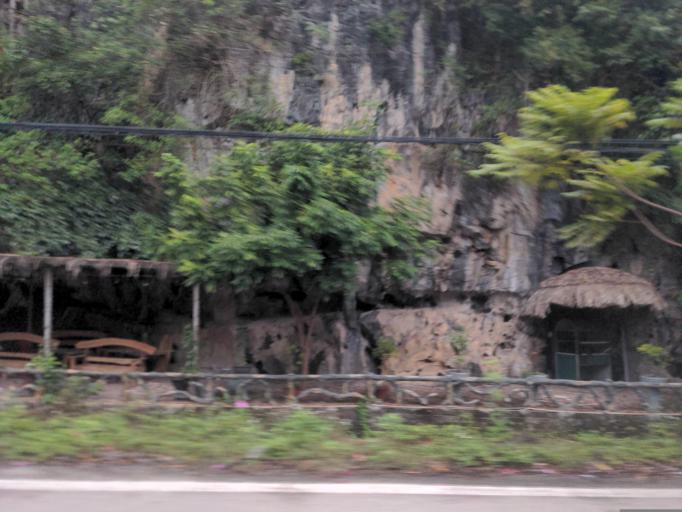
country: VN
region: Ninh Binh
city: Thanh Pho Ninh Binh
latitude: 20.2197
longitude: 105.9289
